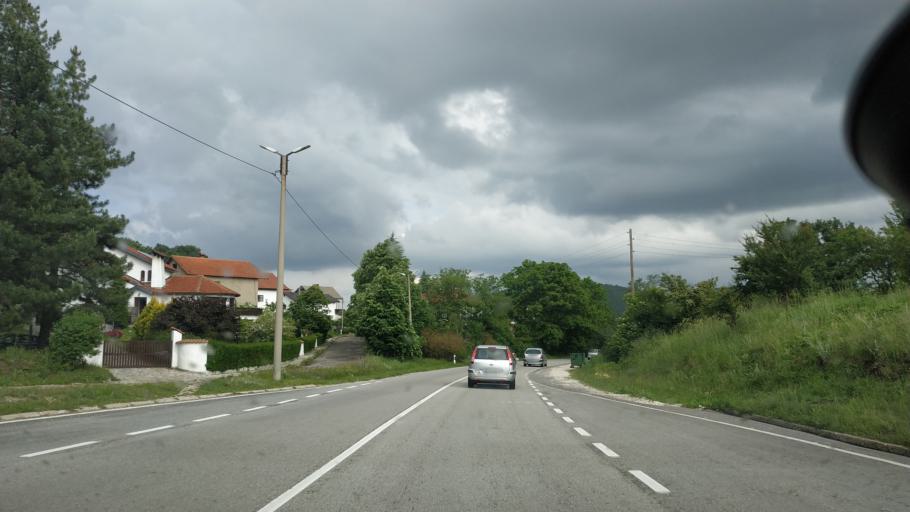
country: RS
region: Central Serbia
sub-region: Borski Okrug
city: Bor
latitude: 44.0602
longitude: 22.0517
